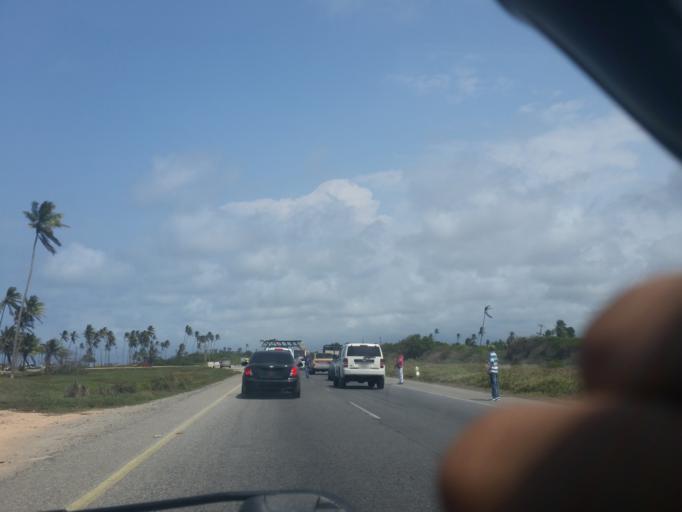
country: VE
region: Carabobo
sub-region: Municipio Juan Jose Mora
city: Moron
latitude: 10.6035
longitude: -68.2564
